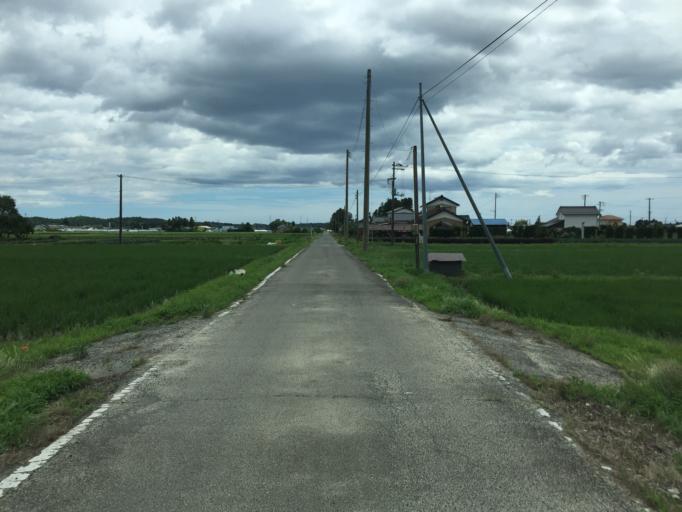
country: JP
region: Fukushima
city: Namie
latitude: 37.6501
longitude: 140.9725
